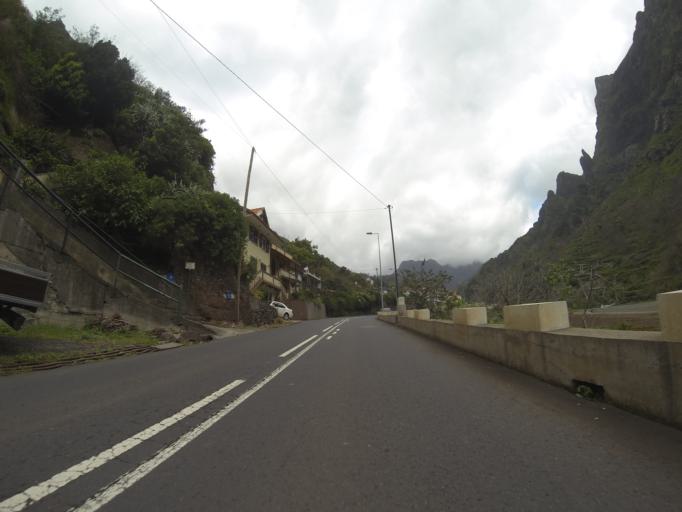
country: PT
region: Madeira
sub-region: Ribeira Brava
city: Campanario
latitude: 32.7192
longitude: -17.0318
